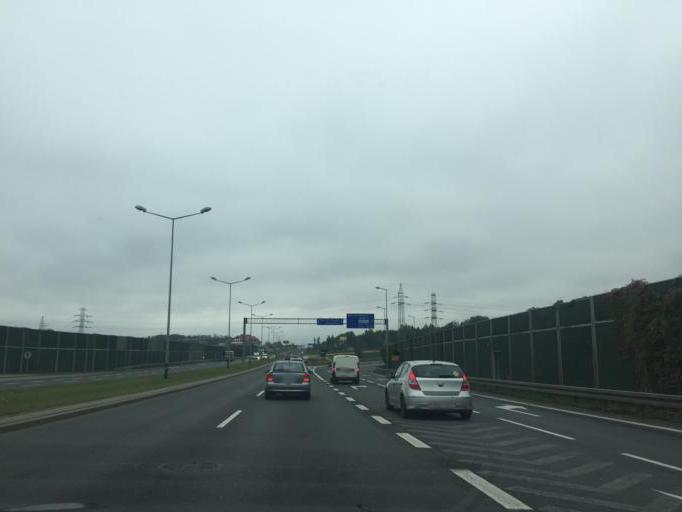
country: PL
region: Lesser Poland Voivodeship
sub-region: Powiat wielicki
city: Czarnochowice
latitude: 50.0069
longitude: 20.0158
